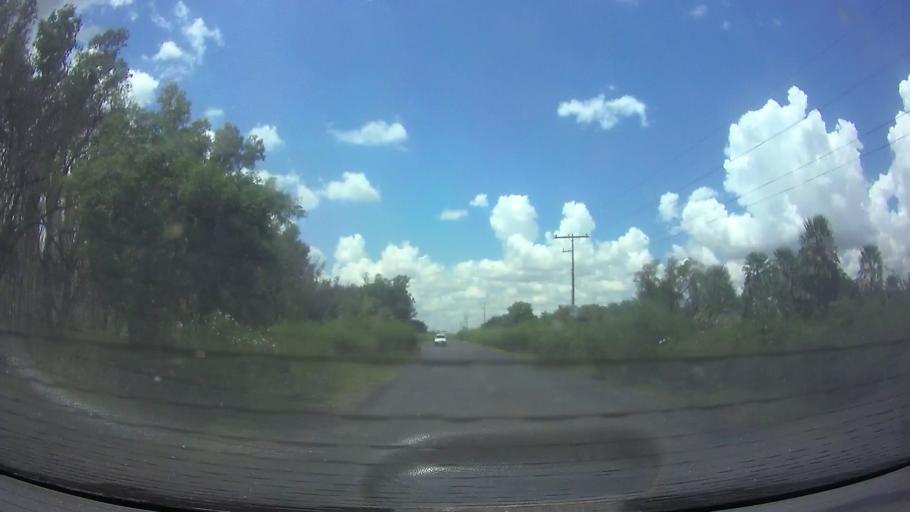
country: PY
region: Presidente Hayes
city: Nanawa
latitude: -25.2461
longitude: -57.6743
